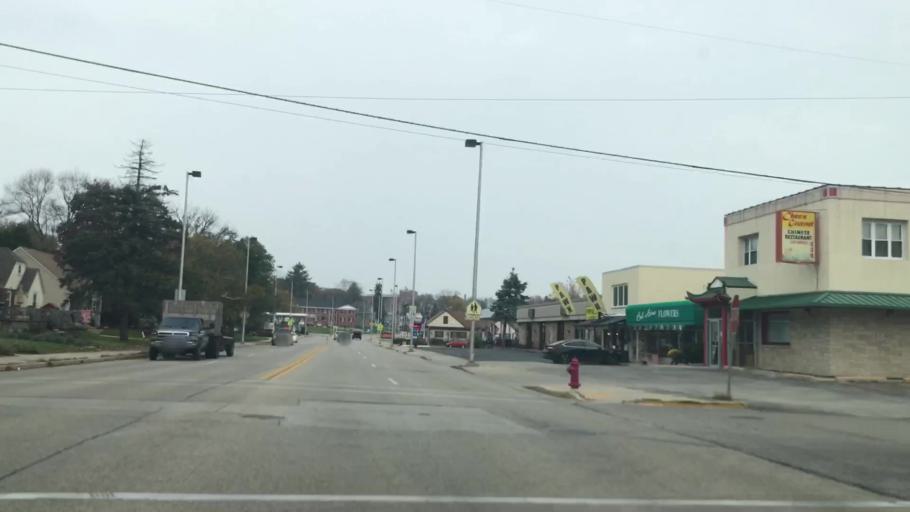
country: US
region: Wisconsin
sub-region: Waukesha County
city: Menomonee Falls
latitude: 43.1730
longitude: -88.1102
